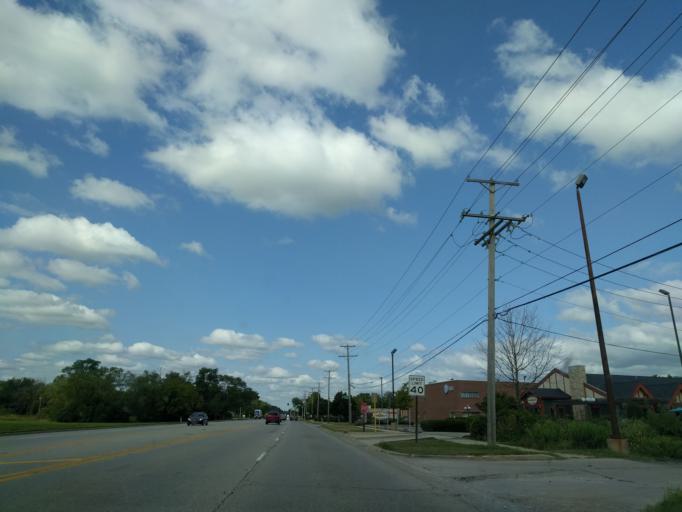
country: US
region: Illinois
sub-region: Cook County
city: Elk Grove Village
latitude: 42.0271
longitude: -87.9753
